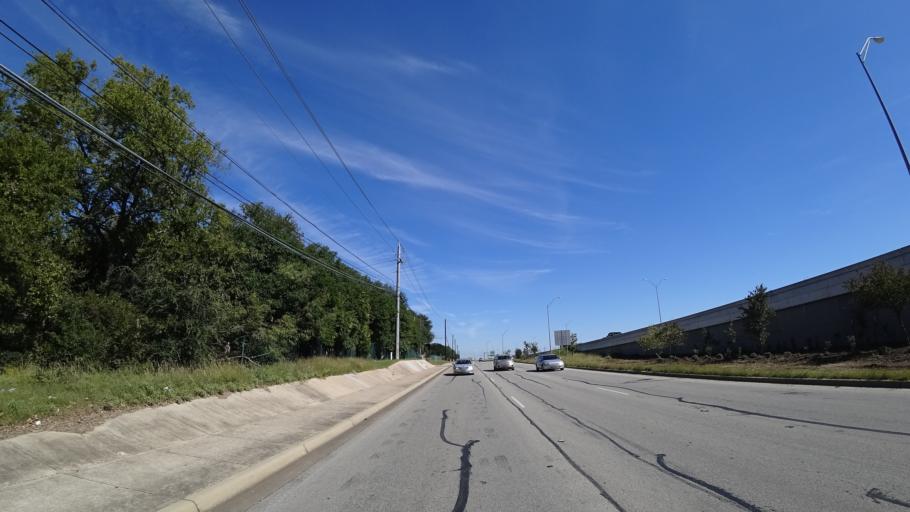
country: US
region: Texas
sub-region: Travis County
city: Austin
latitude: 30.2151
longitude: -97.7311
